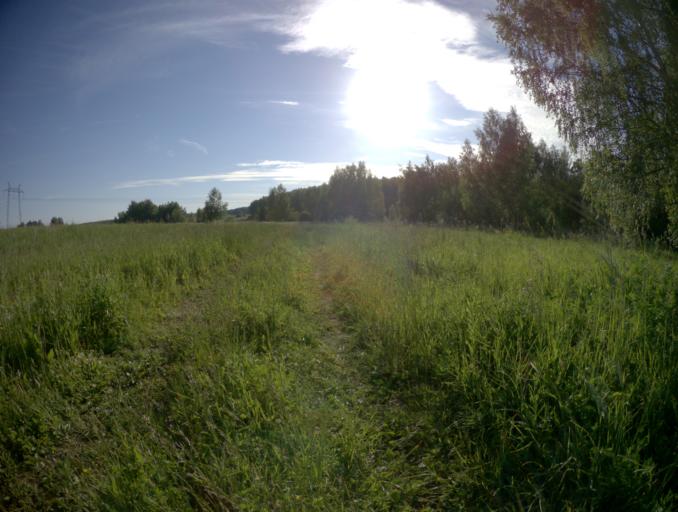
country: RU
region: Vladimir
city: Vorsha
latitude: 56.1411
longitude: 40.2083
